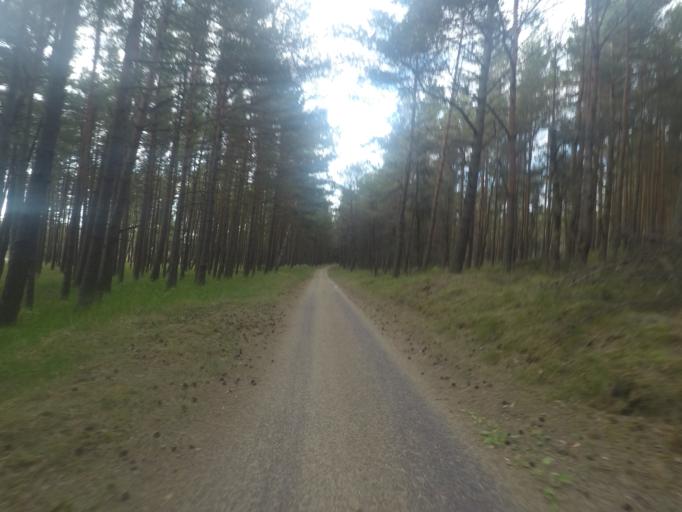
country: LT
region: Klaipedos apskritis
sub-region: Klaipeda
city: Klaipeda
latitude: 55.6597
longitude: 21.1069
